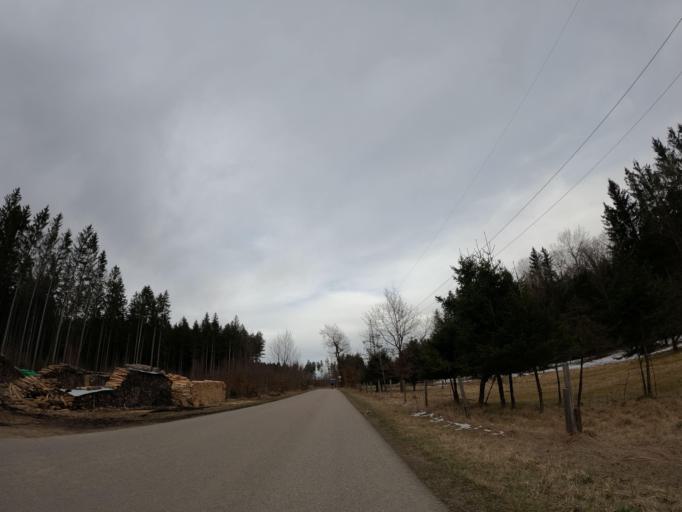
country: DE
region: Bavaria
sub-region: Upper Bavaria
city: Oberhaching
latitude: 48.0108
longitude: 11.5668
